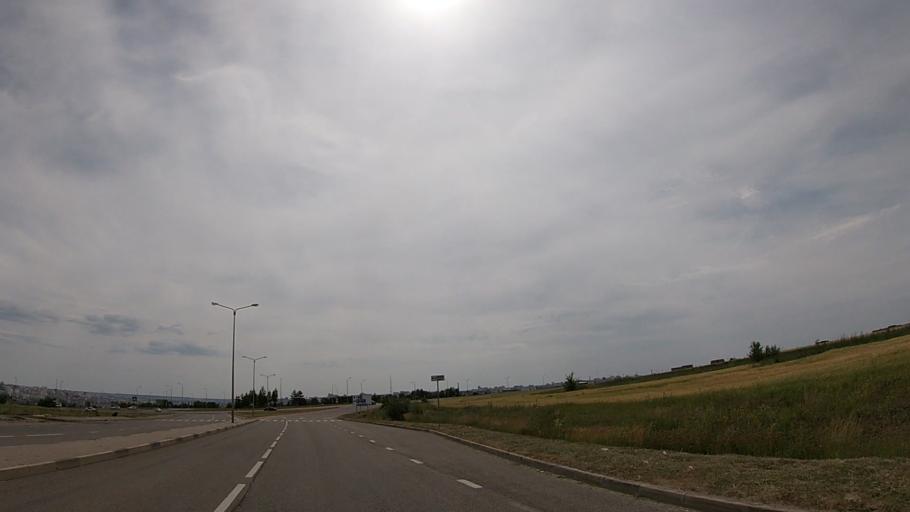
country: RU
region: Belgorod
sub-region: Belgorodskiy Rayon
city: Belgorod
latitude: 50.5937
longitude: 36.5290
